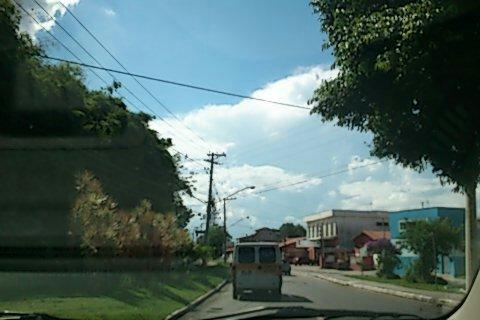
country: BR
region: Sao Paulo
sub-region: Sao Jose Dos Campos
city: Sao Jose dos Campos
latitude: -23.2096
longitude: -45.8572
